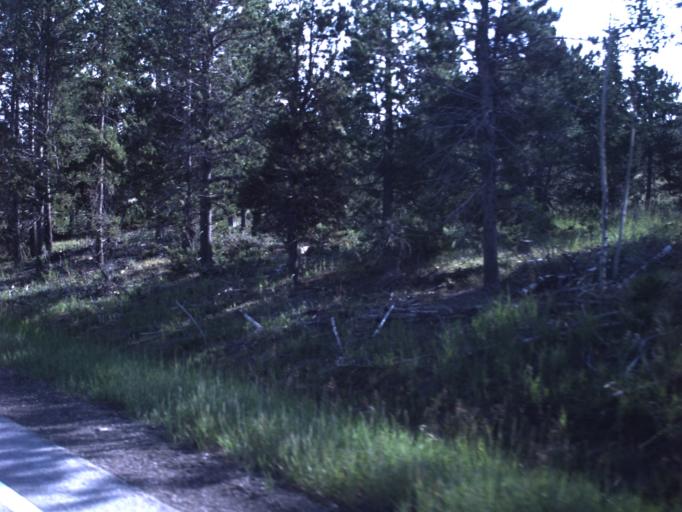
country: US
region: Utah
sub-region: Uintah County
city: Maeser
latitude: 40.7673
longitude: -109.4706
